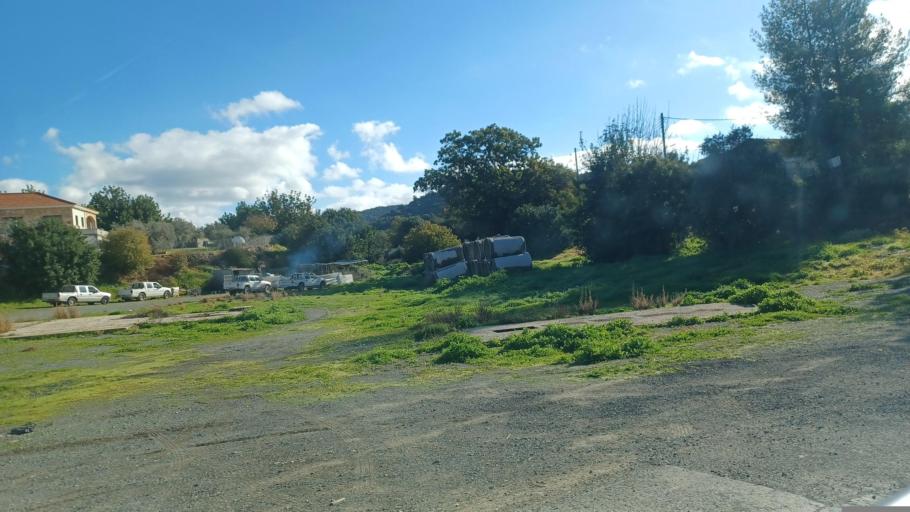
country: CY
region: Limassol
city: Pano Polemidia
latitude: 34.7622
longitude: 33.0033
